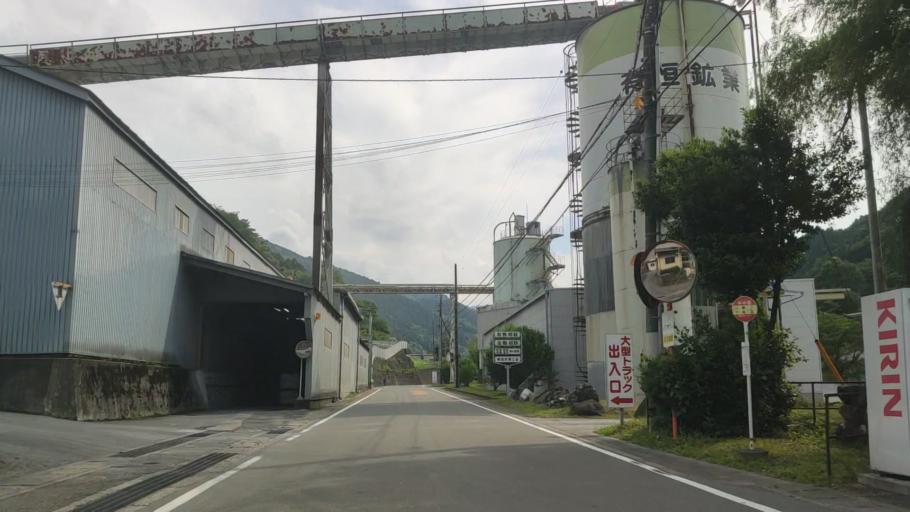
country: JP
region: Gunma
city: Tomioka
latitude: 36.1871
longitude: 138.7491
